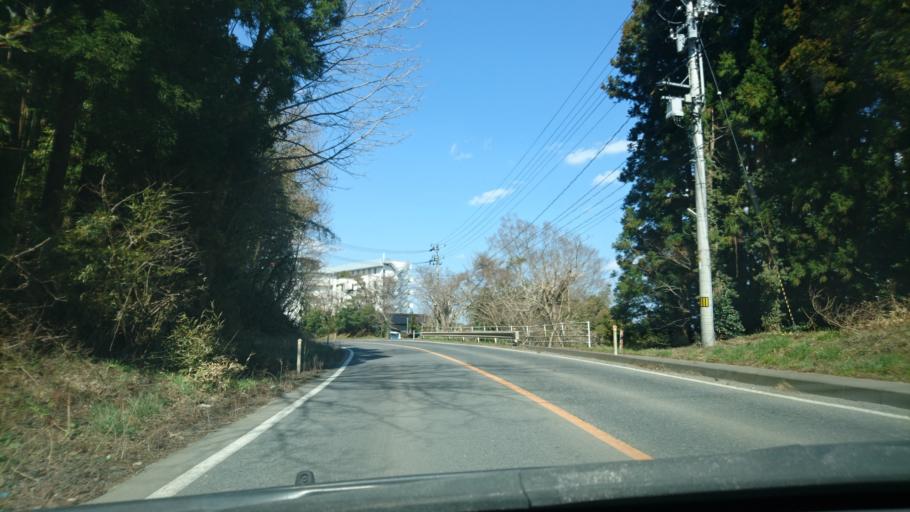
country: JP
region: Miyagi
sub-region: Oshika Gun
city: Onagawa Cho
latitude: 38.6567
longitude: 141.4482
